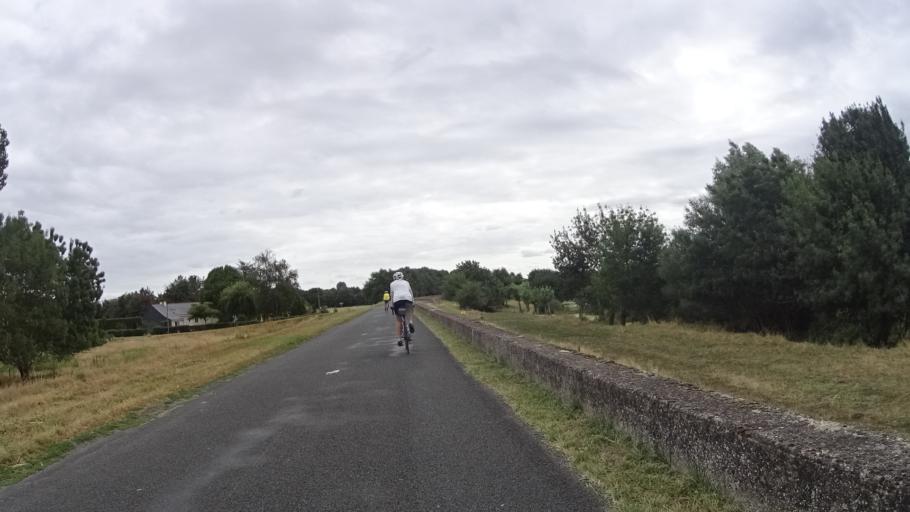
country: FR
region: Pays de la Loire
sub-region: Departement de Maine-et-Loire
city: Chalonnes-sur-Loire
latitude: 47.3641
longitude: -0.7256
